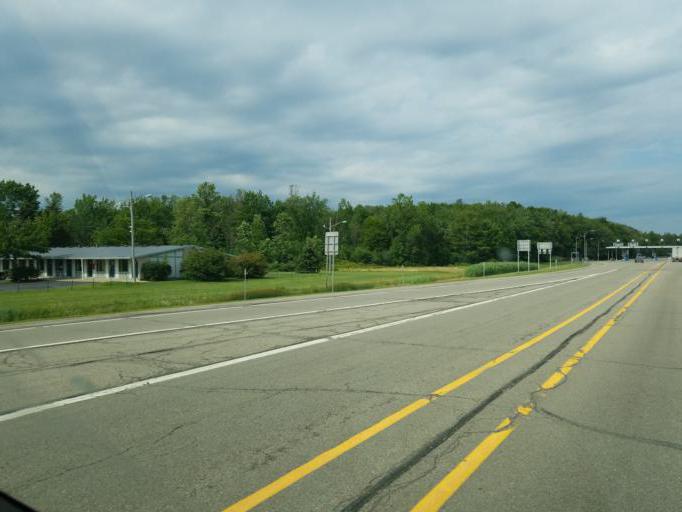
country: US
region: New York
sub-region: Erie County
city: Hamburg
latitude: 42.7436
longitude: -78.8471
